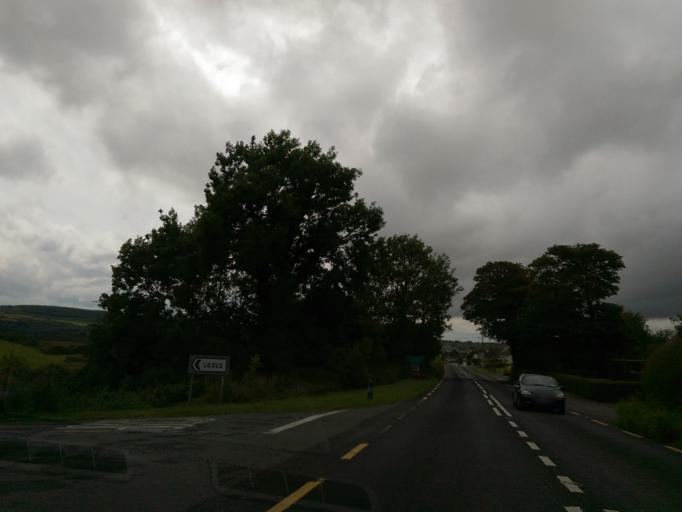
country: IE
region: Munster
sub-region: An Clar
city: Ennis
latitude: 52.7563
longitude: -9.1309
